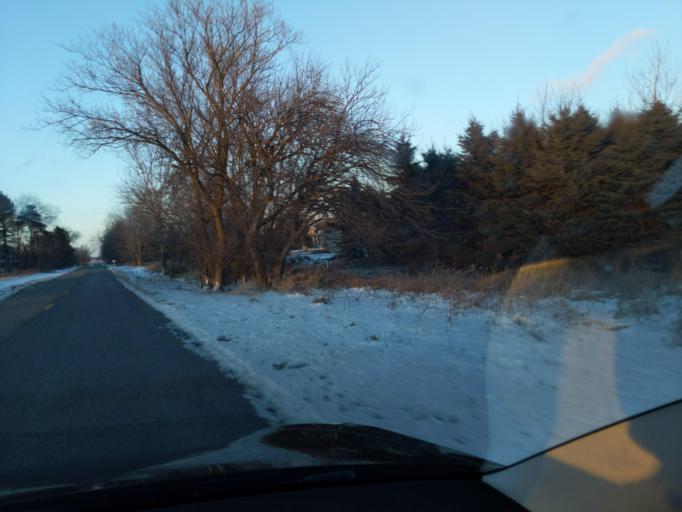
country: US
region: Michigan
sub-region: Ingham County
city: Stockbridge
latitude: 42.4627
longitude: -84.2779
